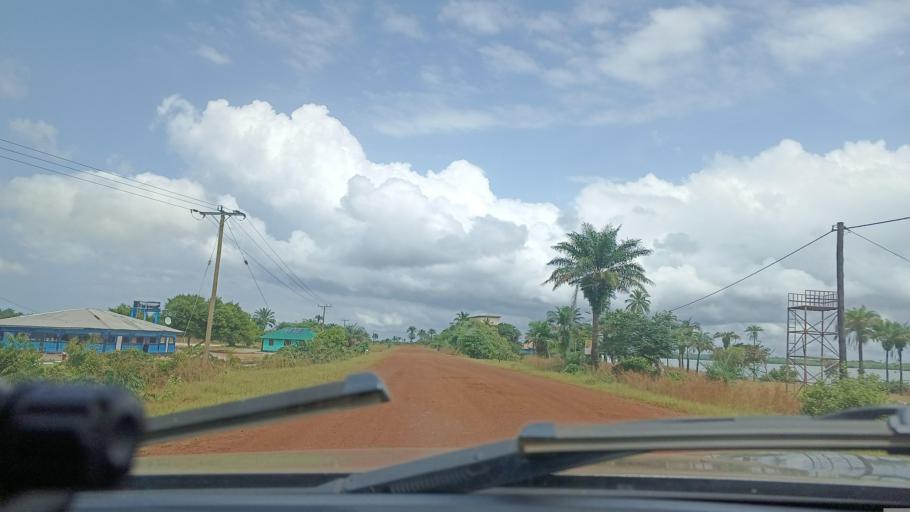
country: LR
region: Grand Cape Mount
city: Robertsport
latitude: 6.7437
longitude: -11.3380
